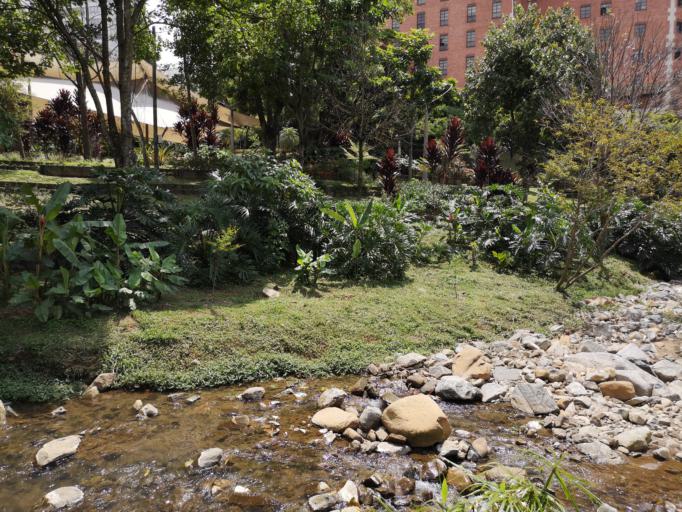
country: CO
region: Antioquia
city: Itagui
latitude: 6.2082
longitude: -75.5708
